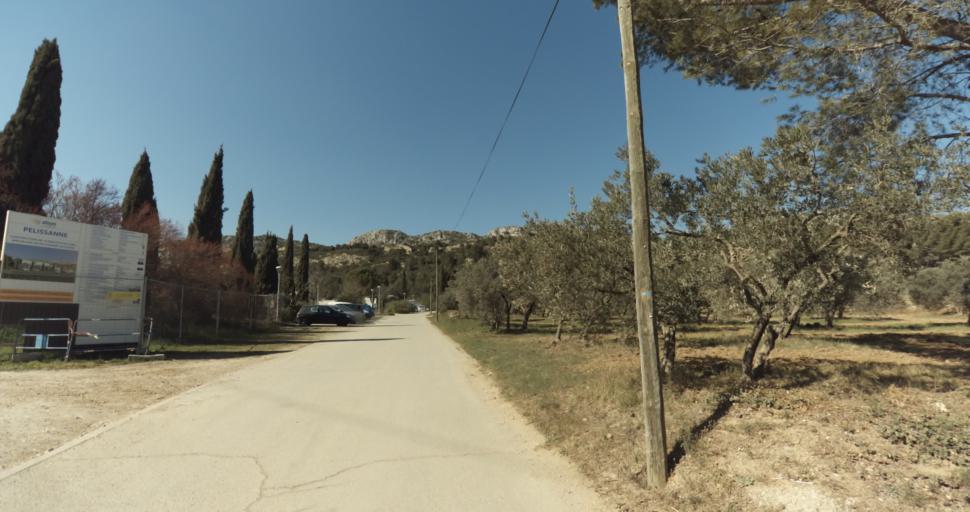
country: FR
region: Provence-Alpes-Cote d'Azur
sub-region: Departement des Bouches-du-Rhone
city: Pelissanne
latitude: 43.6464
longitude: 5.1644
